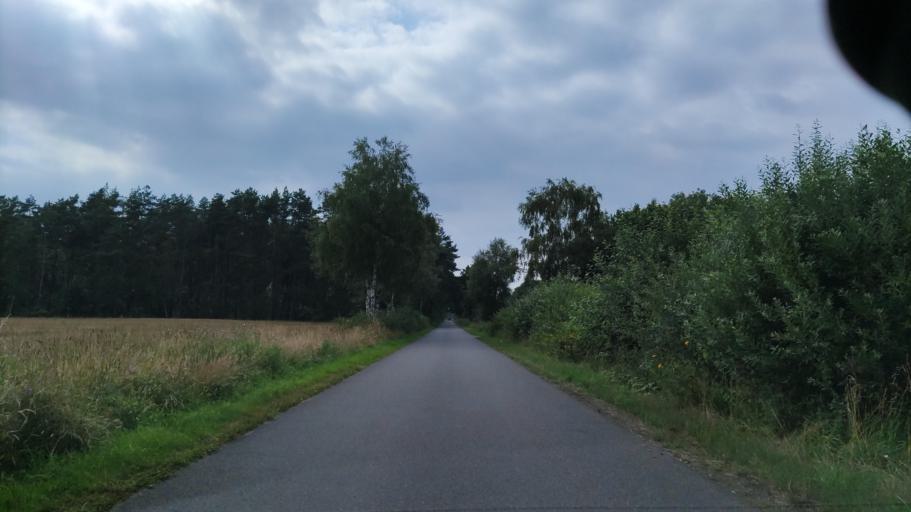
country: DE
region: Lower Saxony
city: Schneverdingen
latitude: 53.0639
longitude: 9.8377
